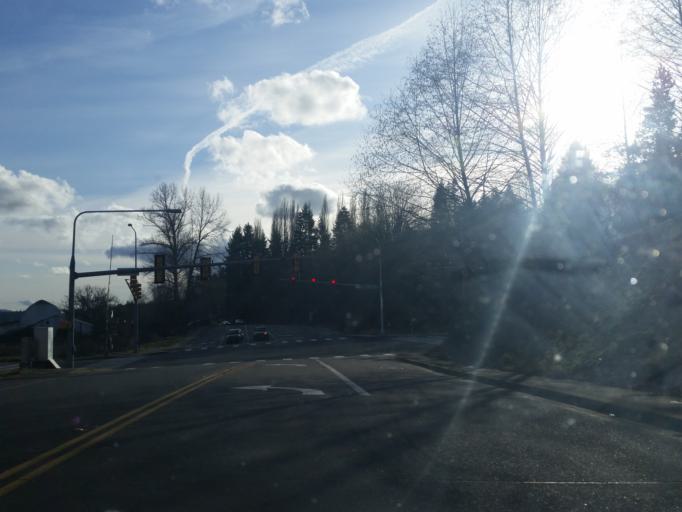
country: US
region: Washington
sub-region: King County
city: Kingsgate
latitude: 47.7120
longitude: -122.1541
